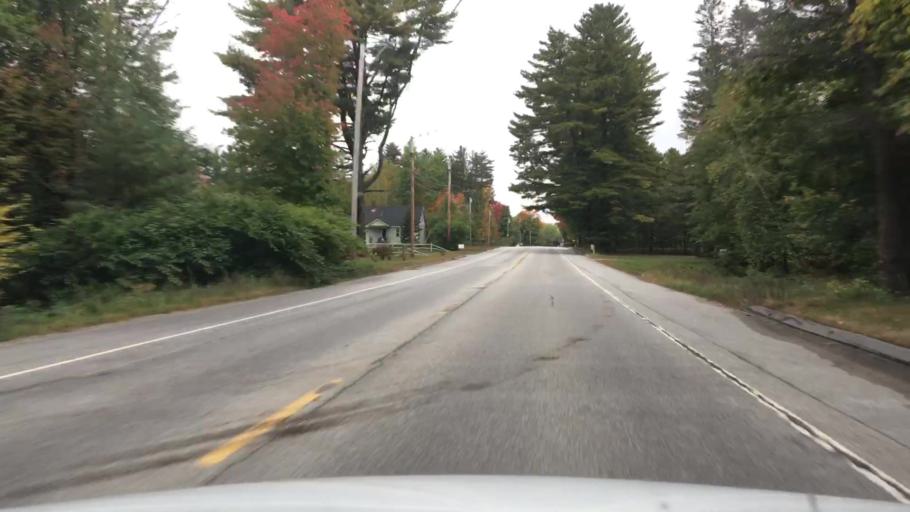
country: US
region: Maine
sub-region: Oxford County
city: Oxford
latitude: 44.1282
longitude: -70.4561
